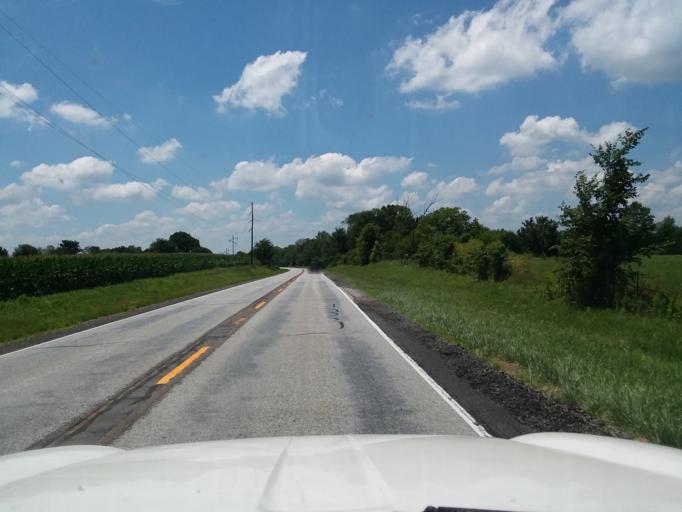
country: US
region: Indiana
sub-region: Johnson County
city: Trafalgar
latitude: 39.4079
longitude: -86.1746
